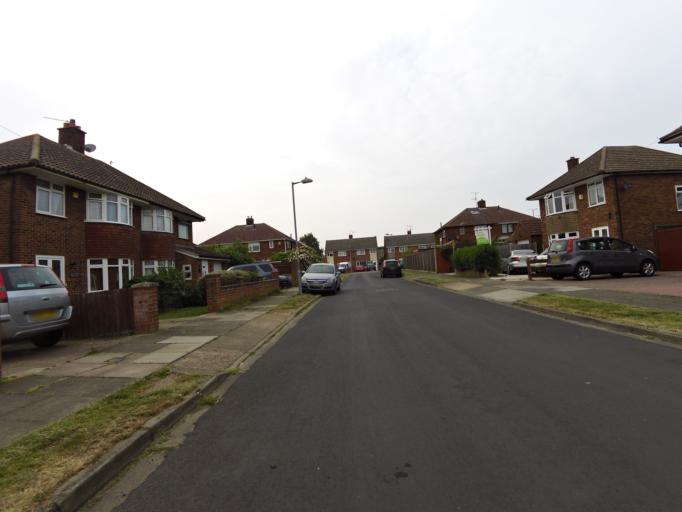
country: GB
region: England
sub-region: Suffolk
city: Ipswich
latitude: 52.0784
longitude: 1.1324
